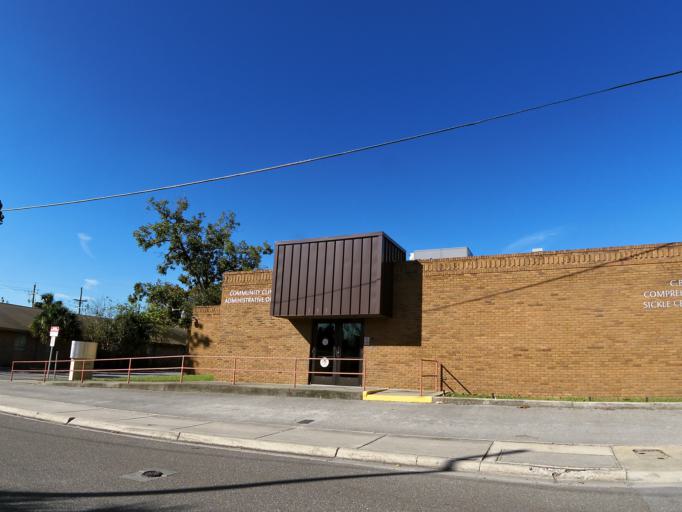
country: US
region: Florida
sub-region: Duval County
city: Jacksonville
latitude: 30.3499
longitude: -81.6617
